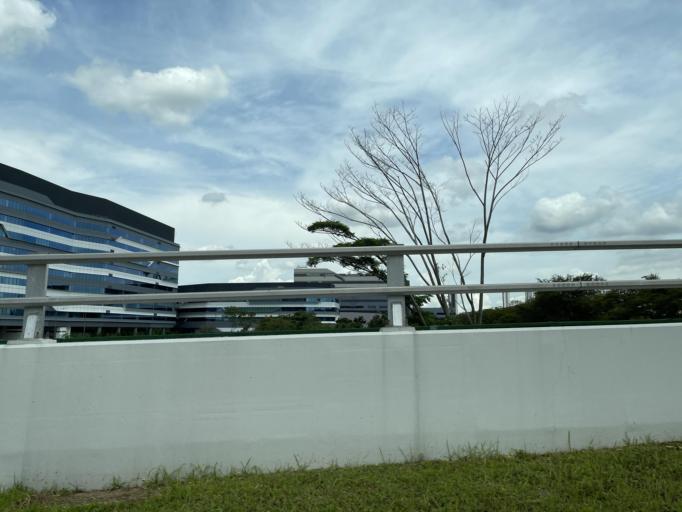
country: SG
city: Singapore
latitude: 1.2898
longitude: 103.7927
